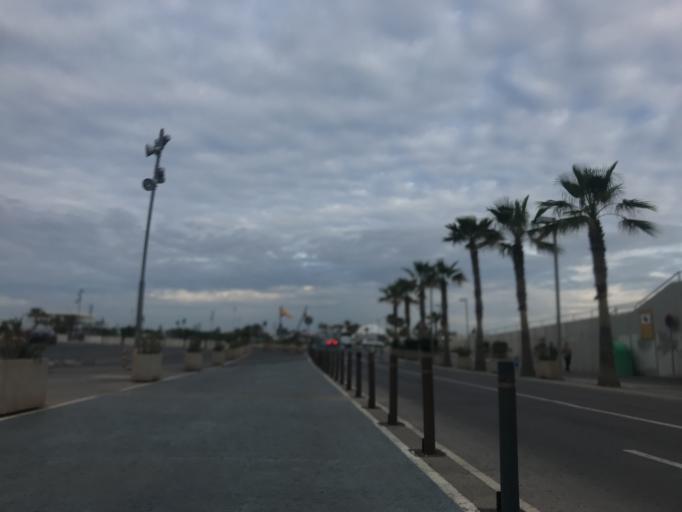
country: ES
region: Valencia
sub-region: Provincia de Valencia
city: Alboraya
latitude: 39.4627
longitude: -0.3182
